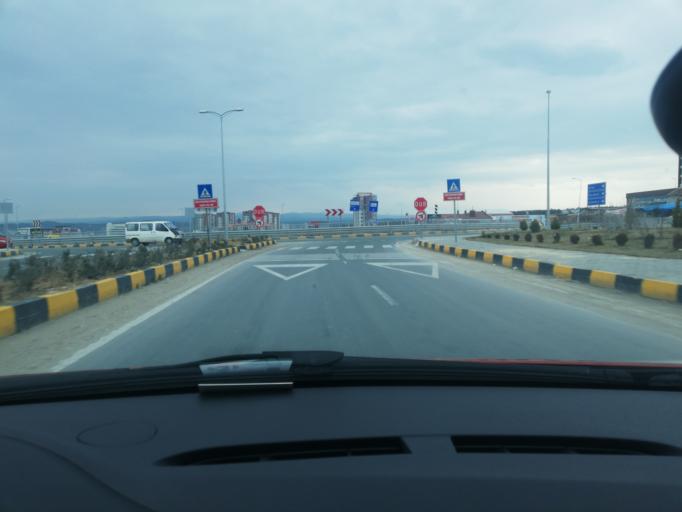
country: TR
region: Kastamonu
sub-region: Cide
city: Kastamonu
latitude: 41.4195
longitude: 33.7753
